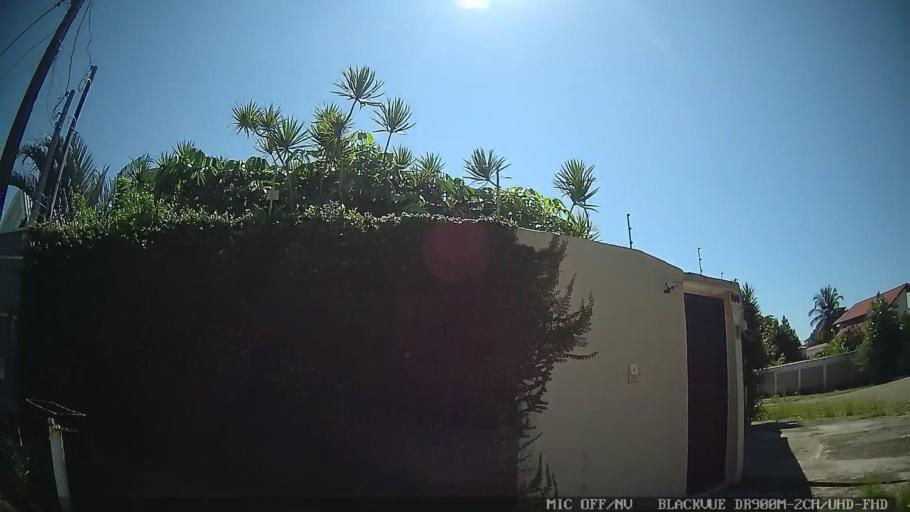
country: BR
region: Sao Paulo
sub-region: Peruibe
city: Peruibe
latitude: -24.3039
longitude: -46.9800
